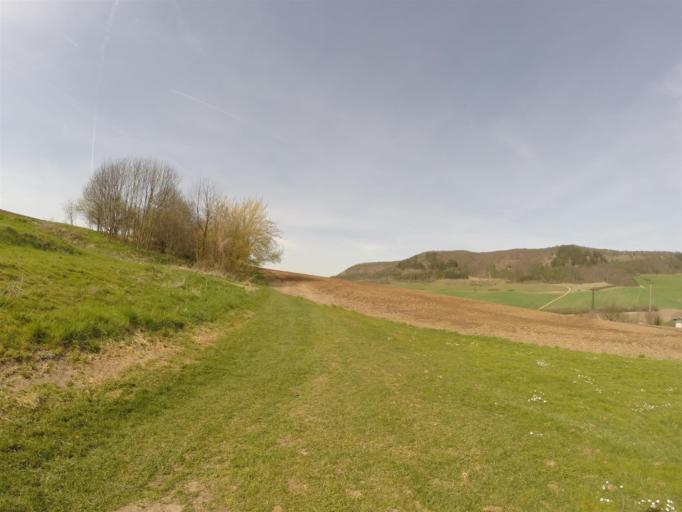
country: DE
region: Thuringia
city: Golmsdorf
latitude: 50.9460
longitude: 11.6539
